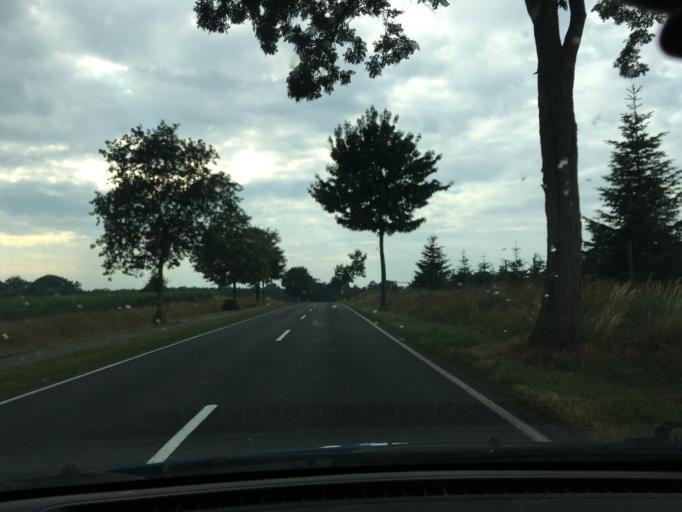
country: DE
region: Lower Saxony
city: Wenzendorf
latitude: 53.3520
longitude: 9.7434
